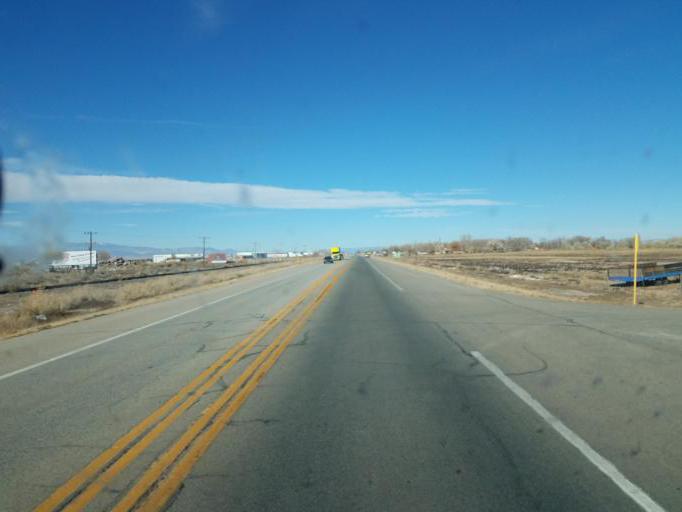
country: US
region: Colorado
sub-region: Alamosa County
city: Alamosa
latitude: 37.4883
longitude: -105.9256
